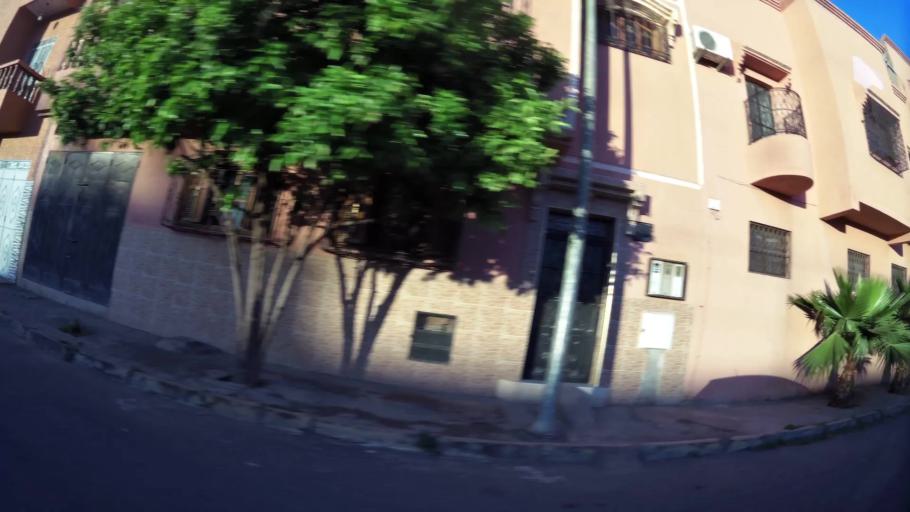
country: MA
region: Marrakech-Tensift-Al Haouz
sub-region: Marrakech
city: Marrakesh
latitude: 31.6373
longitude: -8.0382
